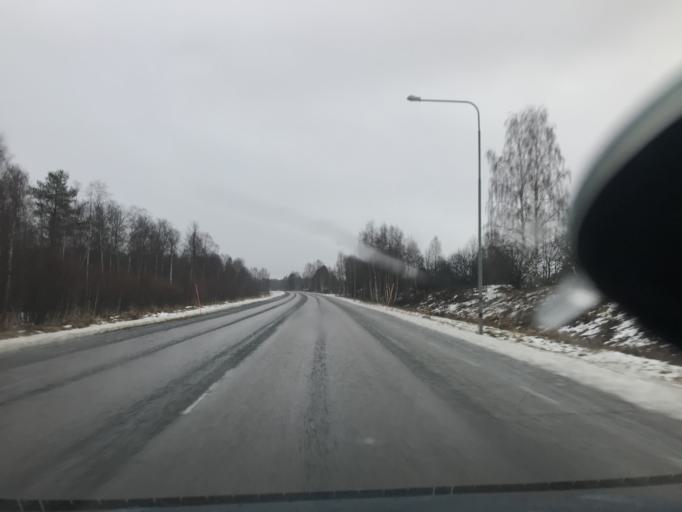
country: SE
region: Norrbotten
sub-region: Lulea Kommun
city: Sodra Sunderbyn
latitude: 65.6584
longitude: 21.9582
